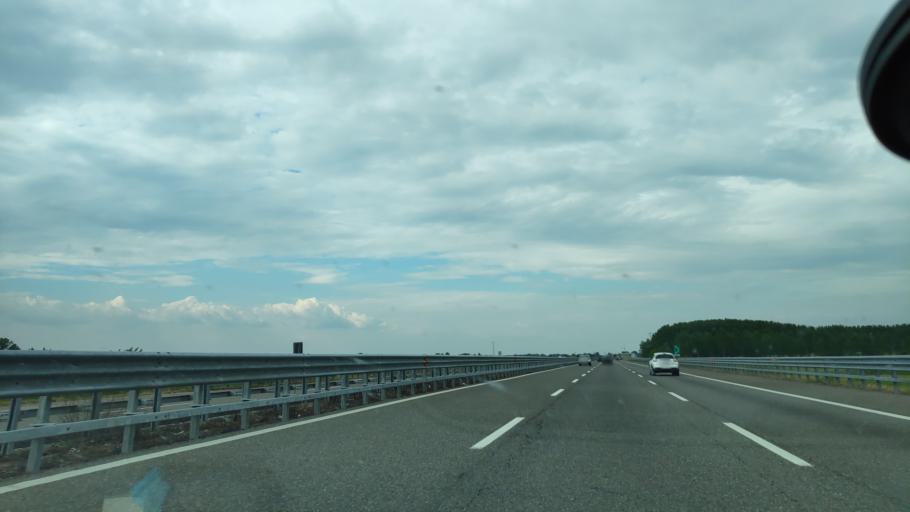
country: IT
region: Lombardy
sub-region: Provincia di Pavia
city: Silvano Pietra
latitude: 45.0524
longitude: 8.9511
